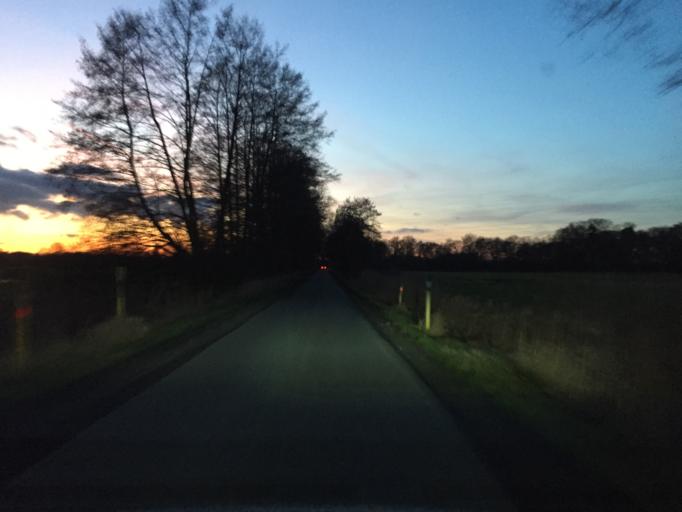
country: DE
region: Lower Saxony
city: Kirchdorf
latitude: 52.6300
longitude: 8.8799
